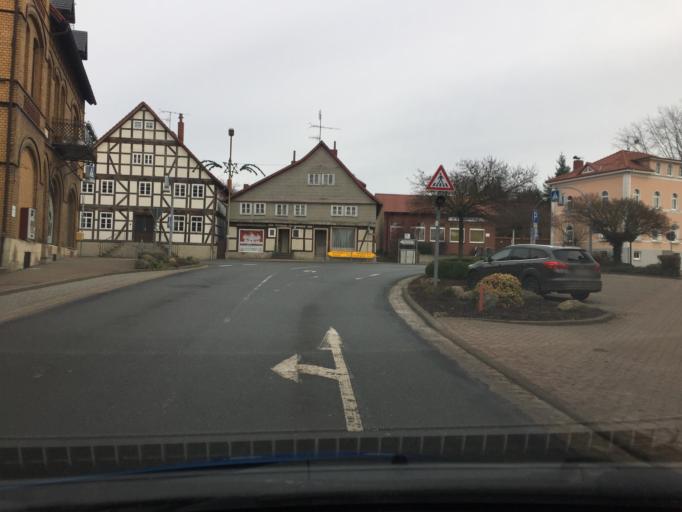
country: DE
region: Lower Saxony
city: Duingen
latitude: 52.0055
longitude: 9.6996
